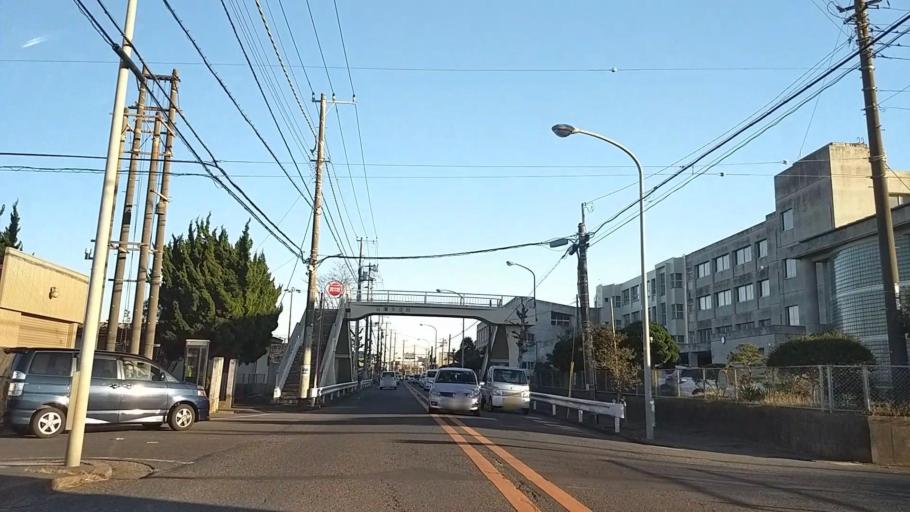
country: JP
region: Chiba
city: Hasaki
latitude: 35.7392
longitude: 140.7998
